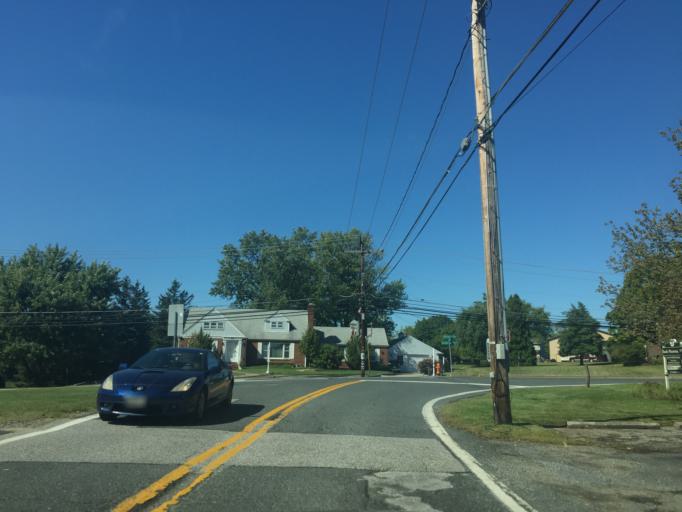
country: US
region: Maryland
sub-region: Baltimore County
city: Rossville
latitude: 39.3614
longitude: -76.4909
